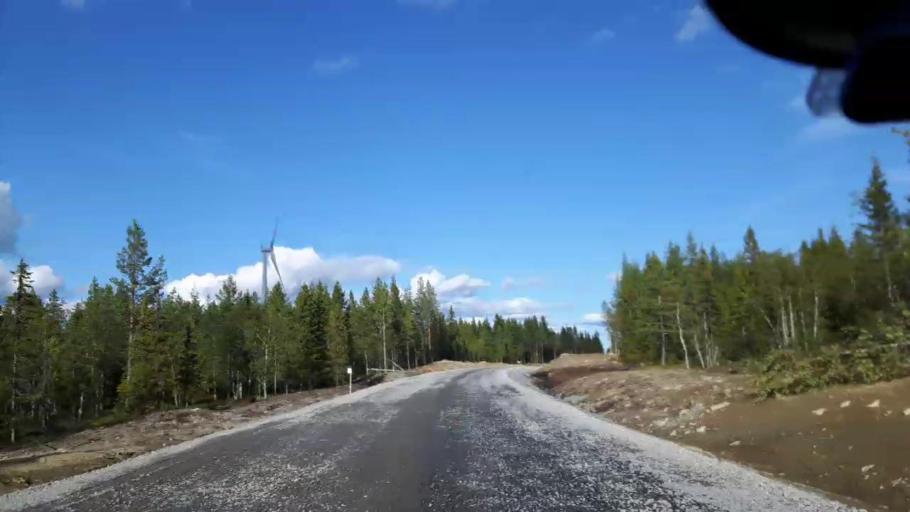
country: SE
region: Jaemtland
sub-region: Ragunda Kommun
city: Hammarstrand
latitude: 63.4232
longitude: 16.1213
